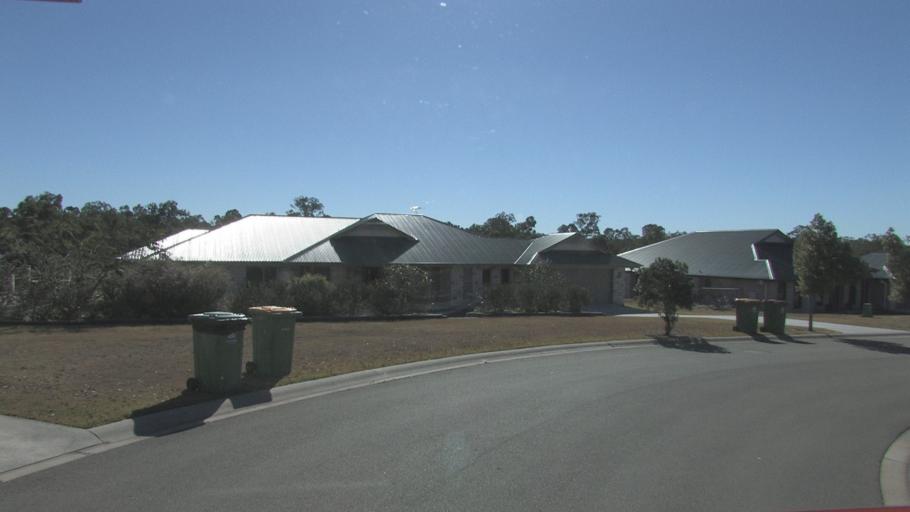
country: AU
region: Queensland
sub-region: Logan
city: North Maclean
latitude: -27.7530
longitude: 152.9636
